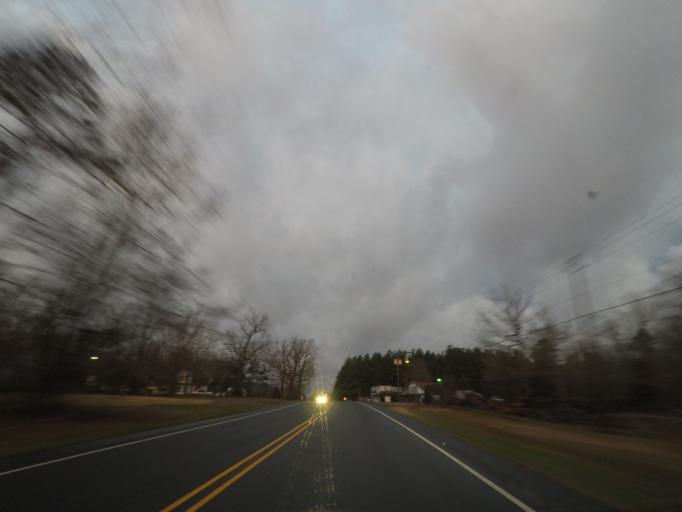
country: US
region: North Carolina
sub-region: Orange County
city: Hillsborough
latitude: 36.2028
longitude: -79.1470
